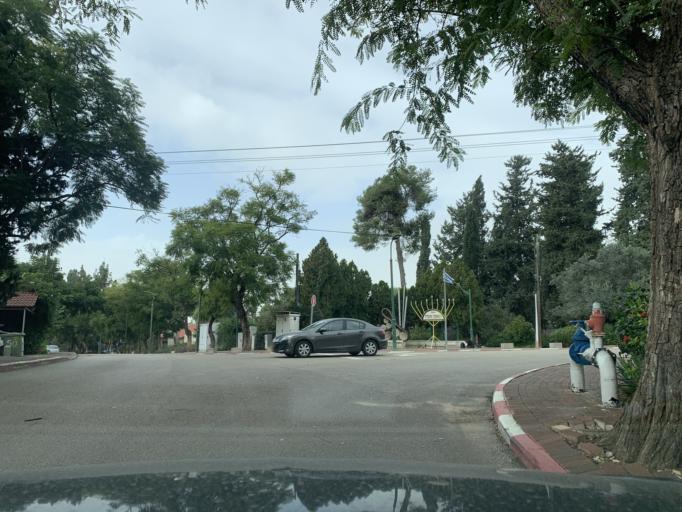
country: IL
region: Central District
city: Jaljulya
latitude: 32.1595
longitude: 34.9444
